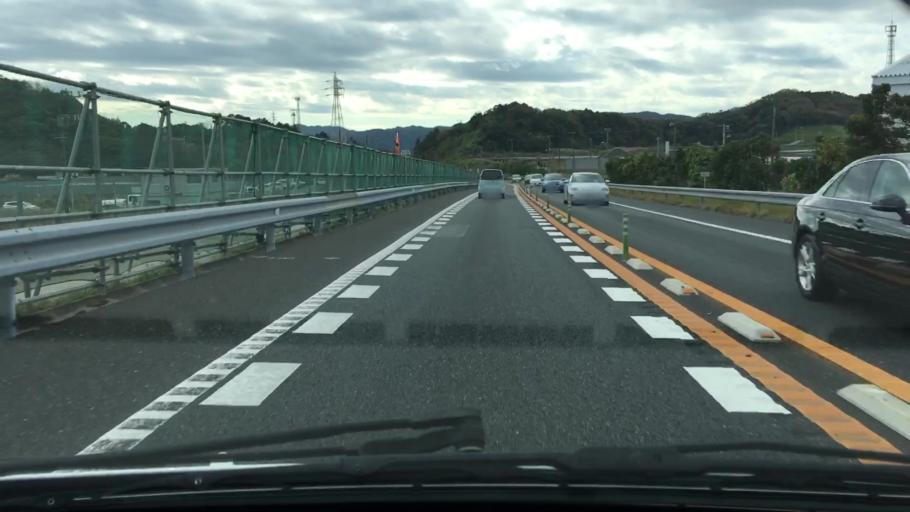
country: JP
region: Chiba
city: Kimitsu
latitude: 35.2339
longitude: 139.8874
